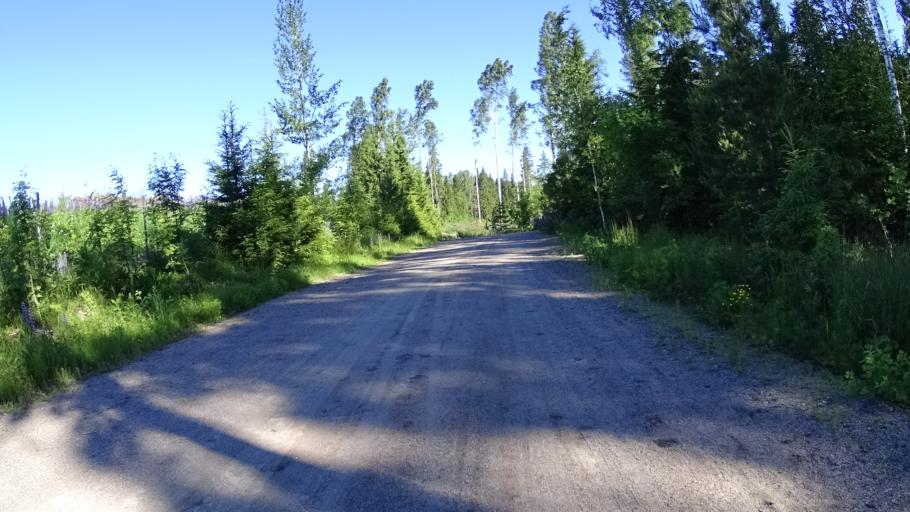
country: FI
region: Uusimaa
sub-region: Helsinki
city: Kilo
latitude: 60.3075
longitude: 24.8109
